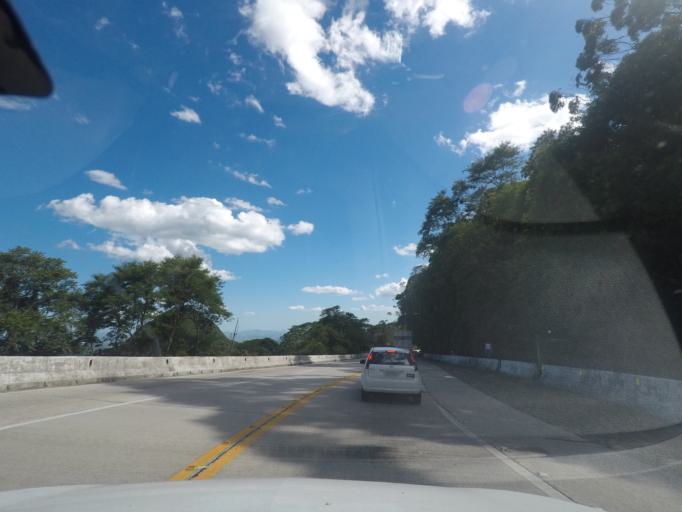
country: BR
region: Rio de Janeiro
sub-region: Guapimirim
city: Guapimirim
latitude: -22.4769
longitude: -42.9953
